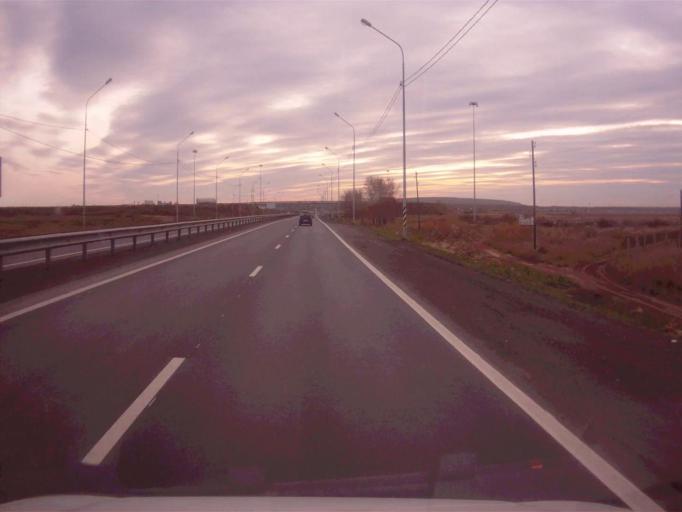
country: RU
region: Chelyabinsk
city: Roza
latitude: 55.0000
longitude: 61.4525
